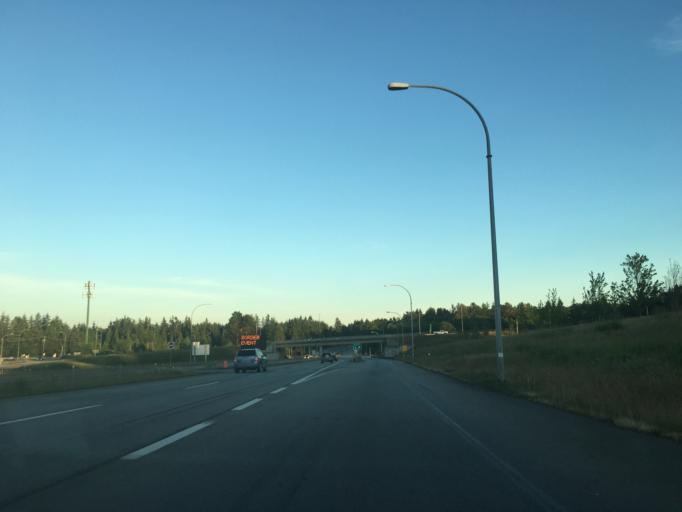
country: US
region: Washington
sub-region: Whatcom County
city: Blaine
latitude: 49.0188
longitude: -122.7610
